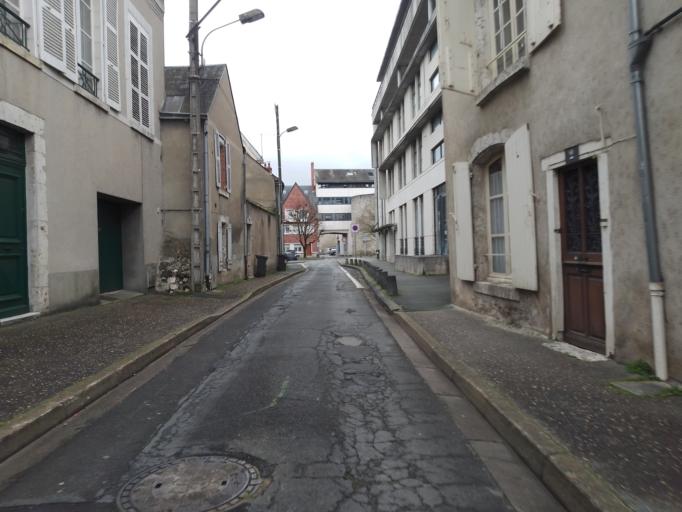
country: FR
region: Centre
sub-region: Departement du Loir-et-Cher
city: Blois
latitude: 47.5900
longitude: 1.3373
